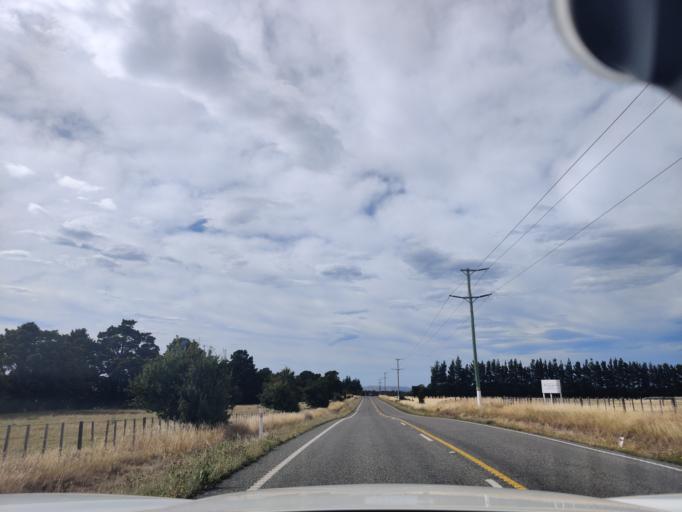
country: NZ
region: Wellington
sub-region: Masterton District
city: Masterton
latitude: -40.8370
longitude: 175.6295
